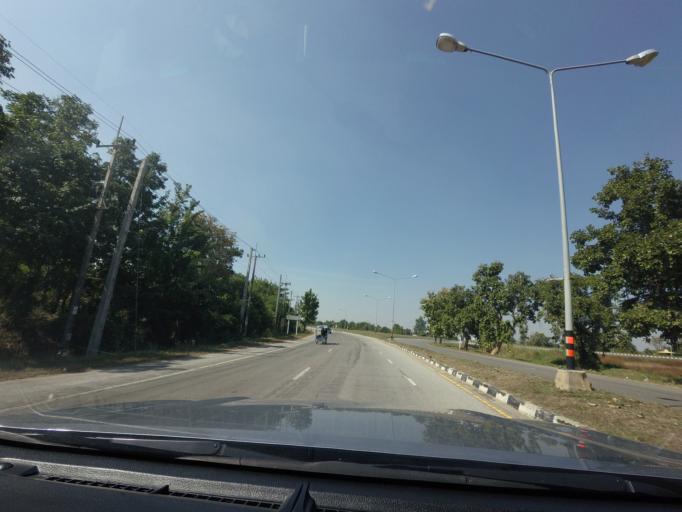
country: TH
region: Sukhothai
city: Ban Na
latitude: 17.0563
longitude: 99.7171
